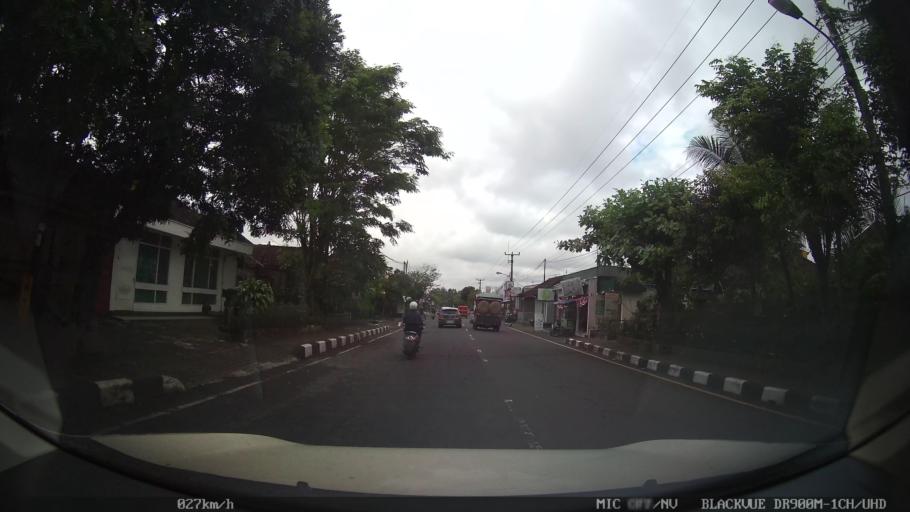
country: ID
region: Bali
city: Banjar Serangan
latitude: -8.5448
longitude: 115.1700
